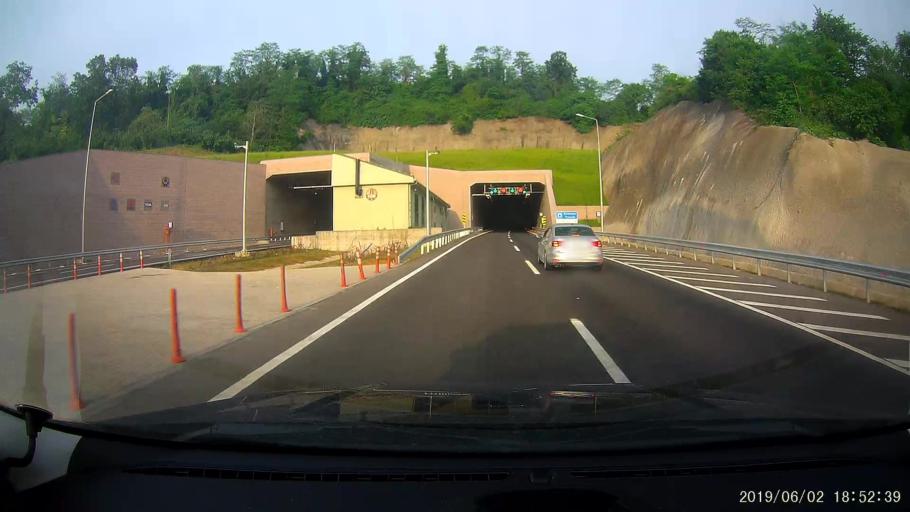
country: TR
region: Ordu
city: Ordu
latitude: 40.9880
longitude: 37.8171
